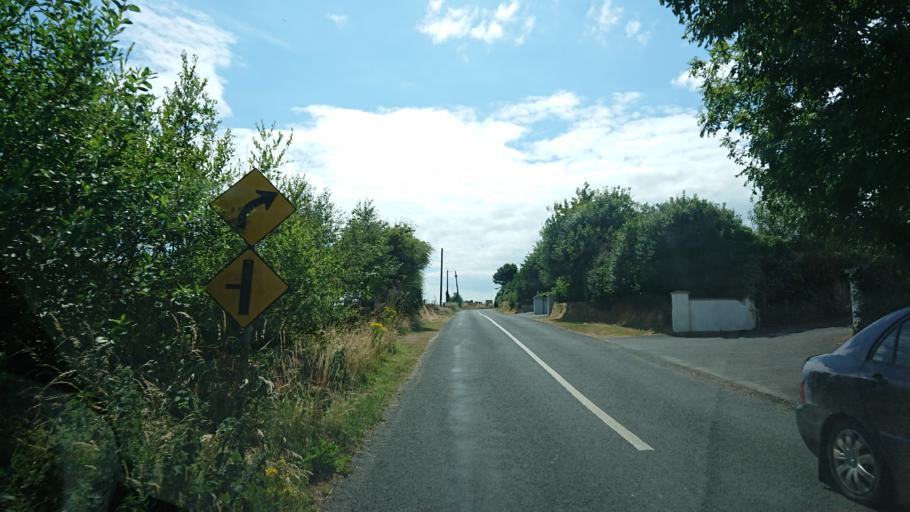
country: IE
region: Munster
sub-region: Waterford
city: Portlaw
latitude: 52.1553
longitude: -7.3455
